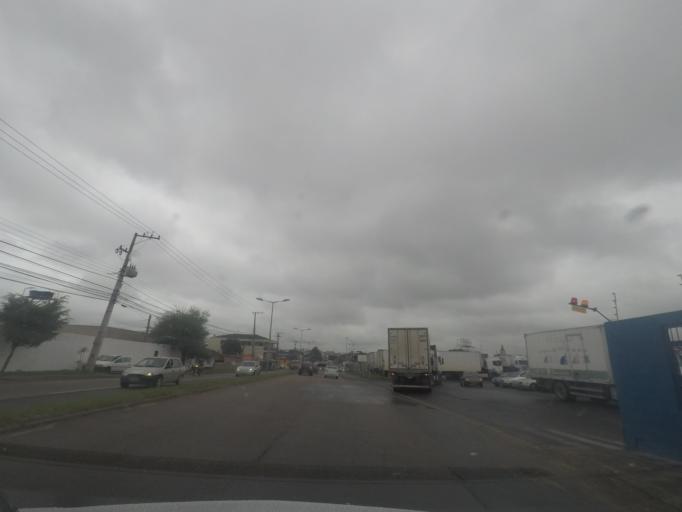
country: BR
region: Parana
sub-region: Pinhais
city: Pinhais
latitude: -25.3906
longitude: -49.1889
